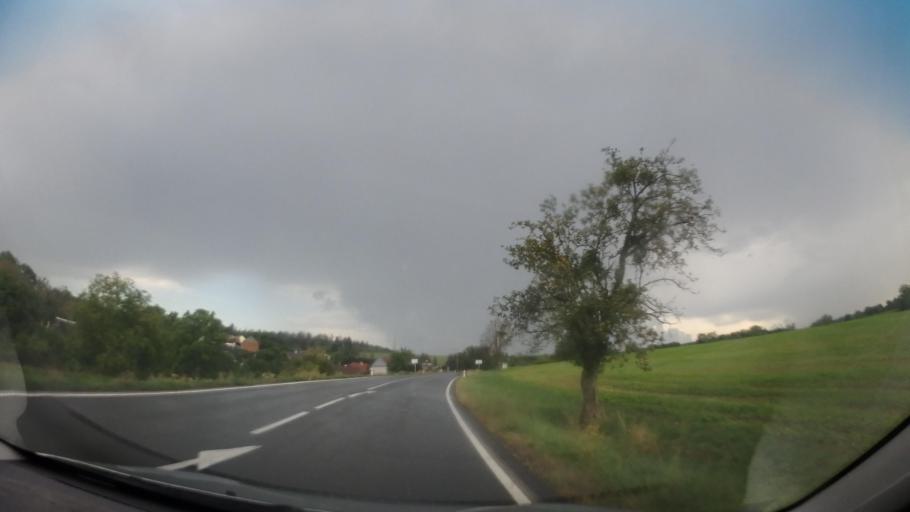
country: CZ
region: Olomoucky
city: Bila Lhota
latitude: 49.7139
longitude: 16.9830
